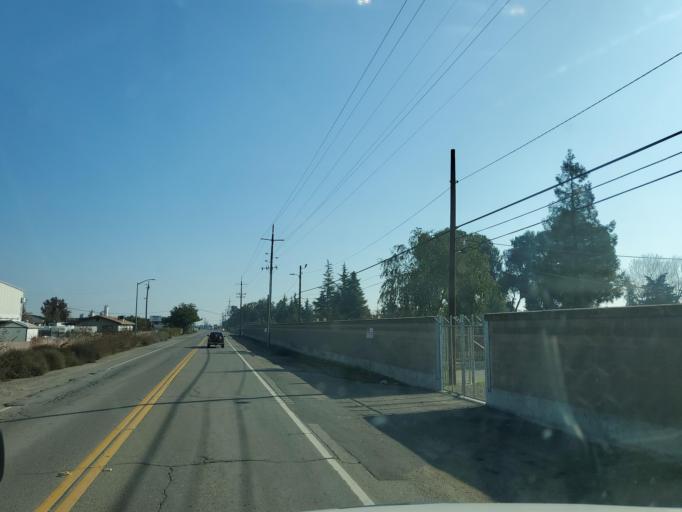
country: US
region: California
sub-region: San Joaquin County
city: French Camp
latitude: 37.8556
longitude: -121.2707
